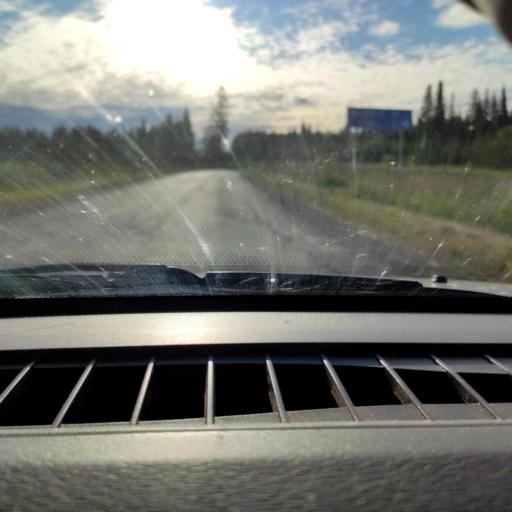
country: RU
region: Perm
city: Uinskoye
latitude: 57.1123
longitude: 56.5335
